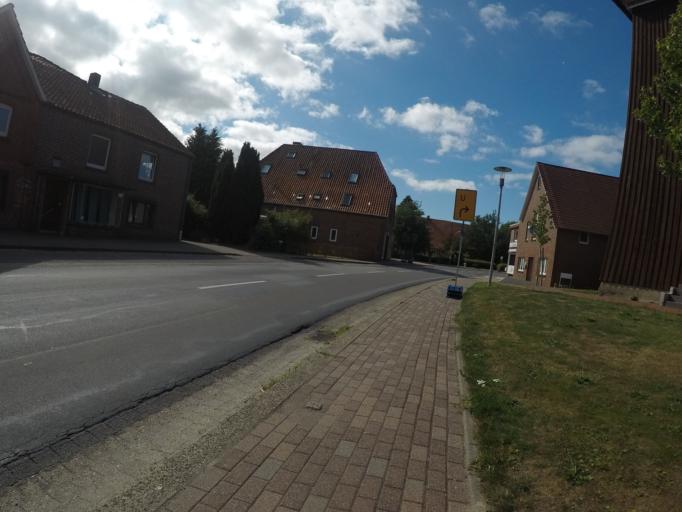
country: DE
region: Lower Saxony
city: Osterbruch
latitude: 53.7778
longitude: 8.9422
